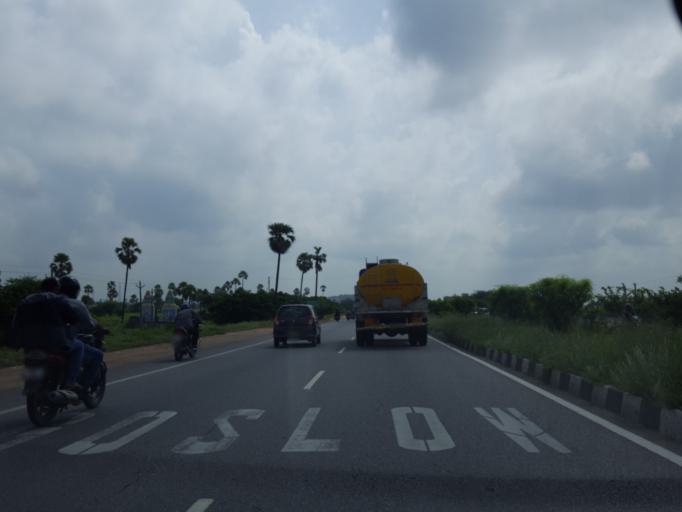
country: IN
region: Telangana
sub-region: Nalgonda
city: Bhongir
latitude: 17.2306
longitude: 78.9680
